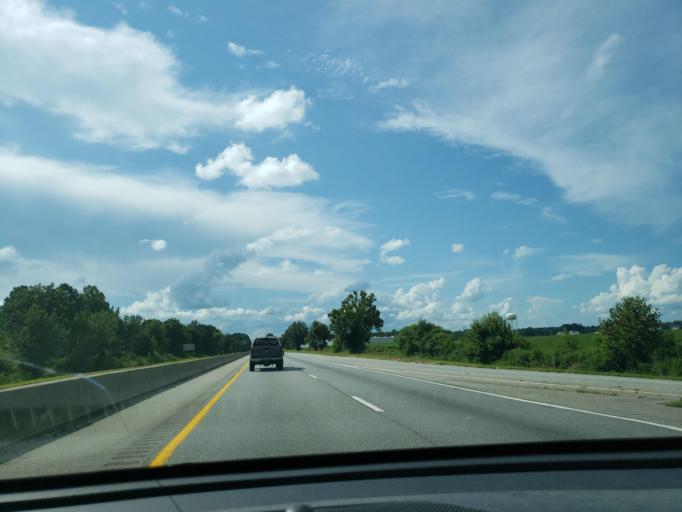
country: US
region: Virginia
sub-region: City of Franklin
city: Franklin
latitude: 36.6521
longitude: -76.9204
